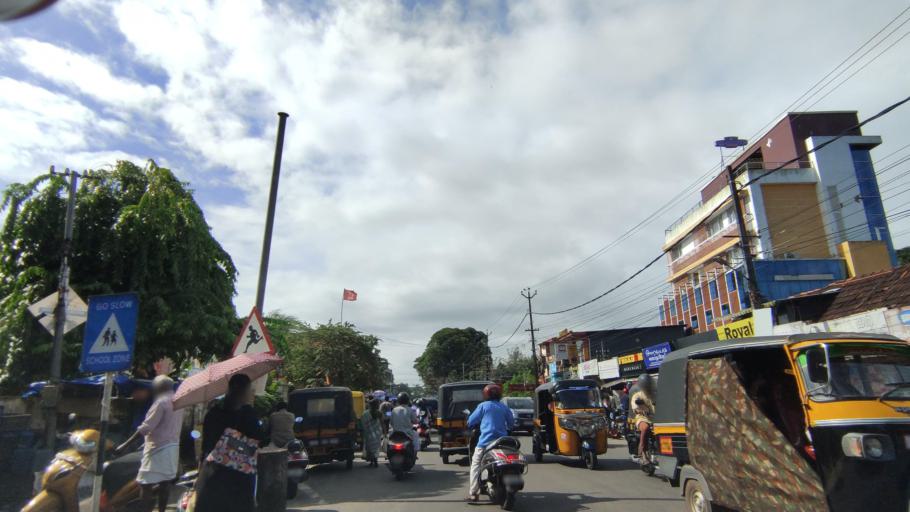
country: IN
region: Kerala
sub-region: Alappuzha
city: Alleppey
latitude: 9.5012
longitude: 76.3419
